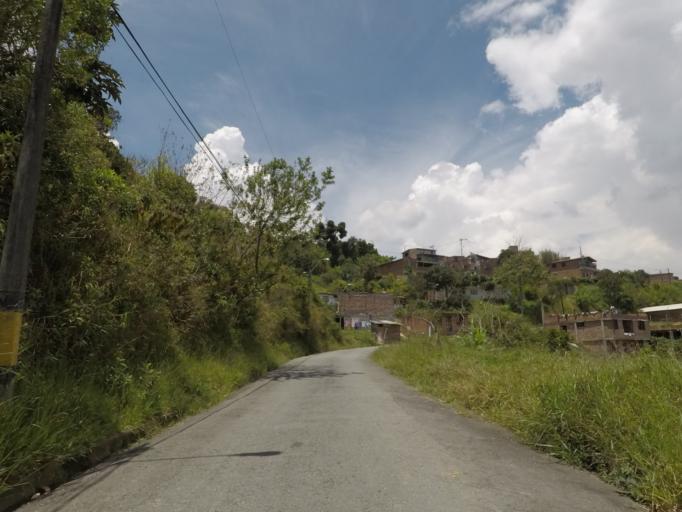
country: CO
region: Antioquia
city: Medellin
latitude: 6.2712
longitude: -75.6361
